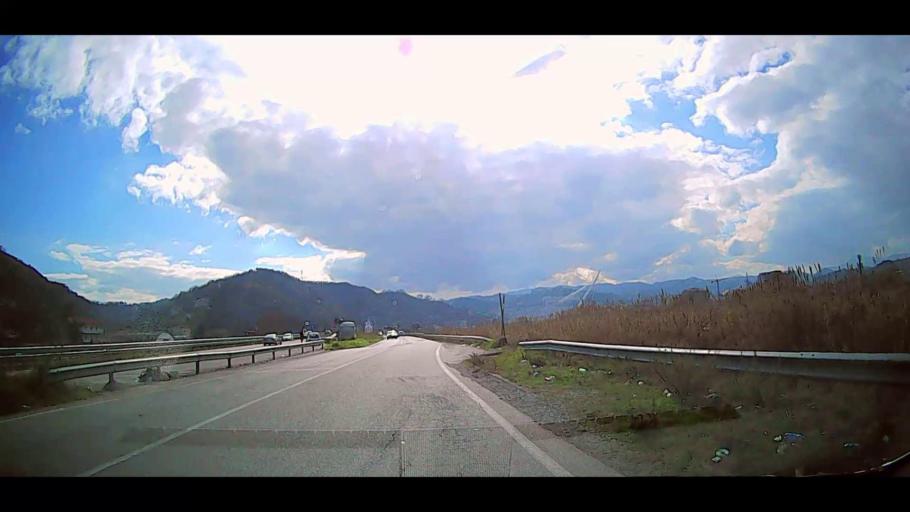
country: IT
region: Calabria
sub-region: Provincia di Cosenza
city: Cosenza
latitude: 39.3075
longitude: 16.2626
